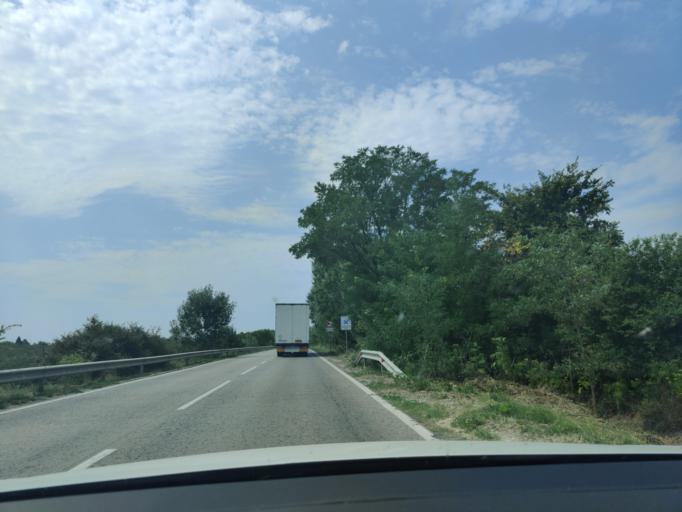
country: BG
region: Vidin
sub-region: Obshtina Vidin
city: Dunavtsi
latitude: 43.8798
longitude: 22.7908
